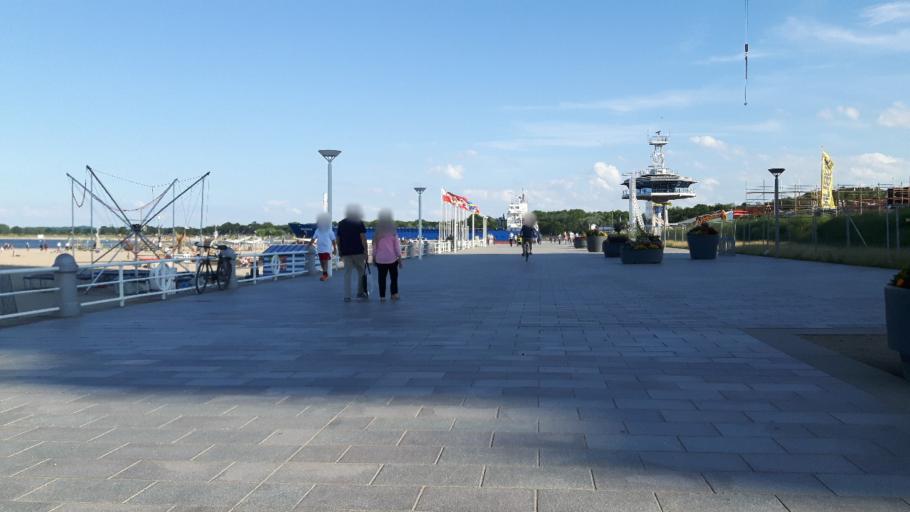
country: DE
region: Schleswig-Holstein
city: Travemuende
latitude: 53.9622
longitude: 10.8826
